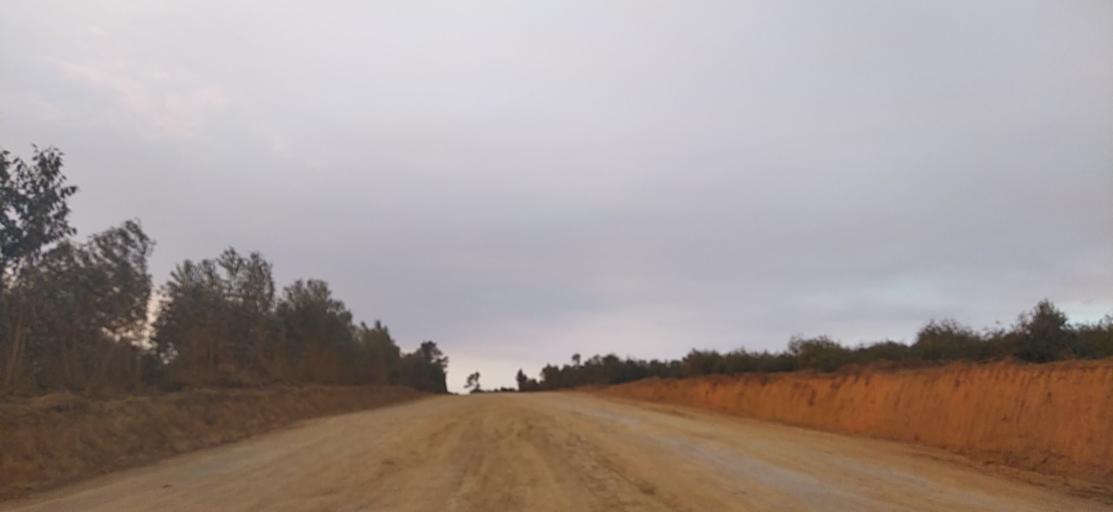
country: MG
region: Analamanga
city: Anjozorobe
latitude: -18.4734
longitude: 48.2620
